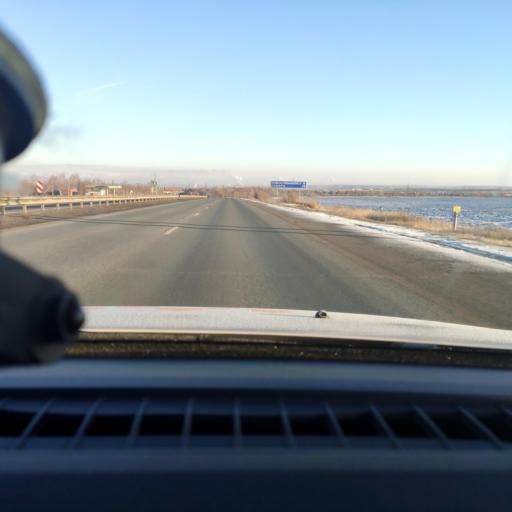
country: RU
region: Samara
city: Novokuybyshevsk
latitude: 53.0136
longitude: 49.9805
